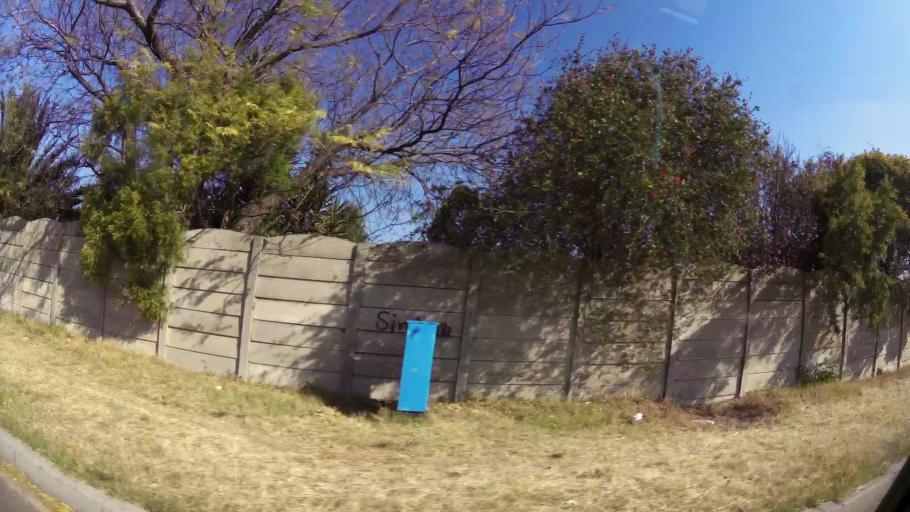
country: ZA
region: Gauteng
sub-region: City of Johannesburg Metropolitan Municipality
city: Johannesburg
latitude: -26.2588
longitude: 28.0167
